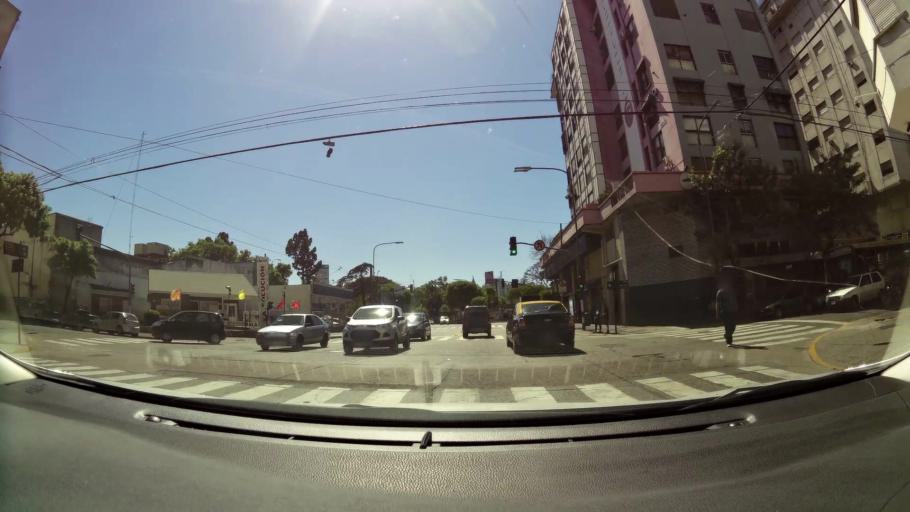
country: AR
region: Buenos Aires F.D.
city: Buenos Aires
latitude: -34.6269
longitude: -58.3830
